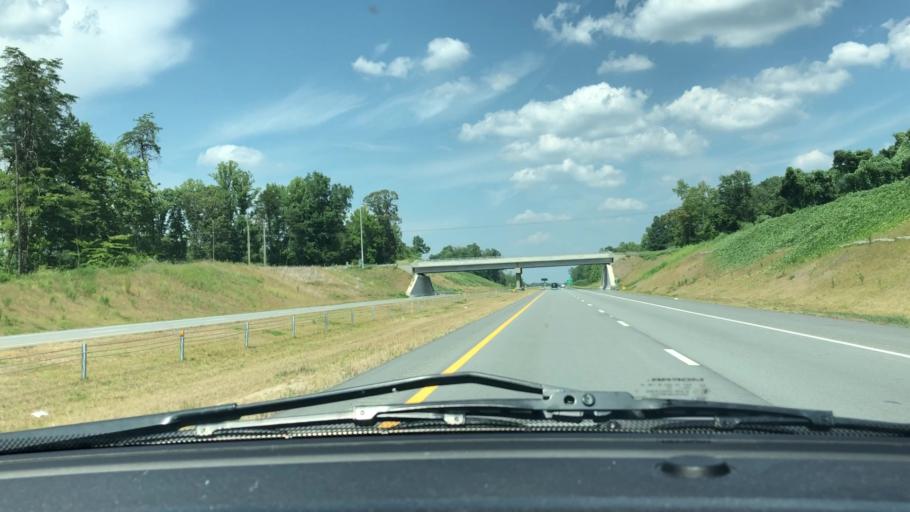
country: US
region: North Carolina
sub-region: Guilford County
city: Oak Ridge
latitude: 36.1684
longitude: -79.9492
